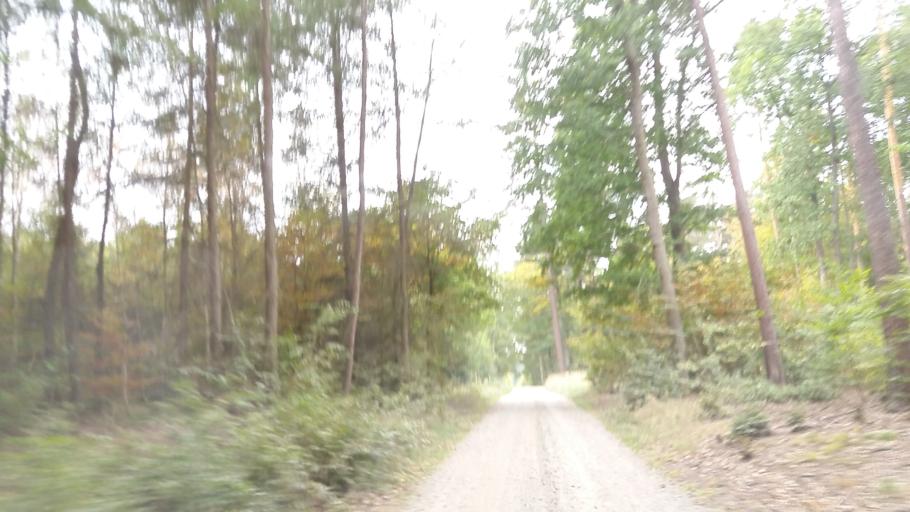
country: PL
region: West Pomeranian Voivodeship
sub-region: Powiat mysliborski
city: Barlinek
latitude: 52.9150
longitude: 15.1969
